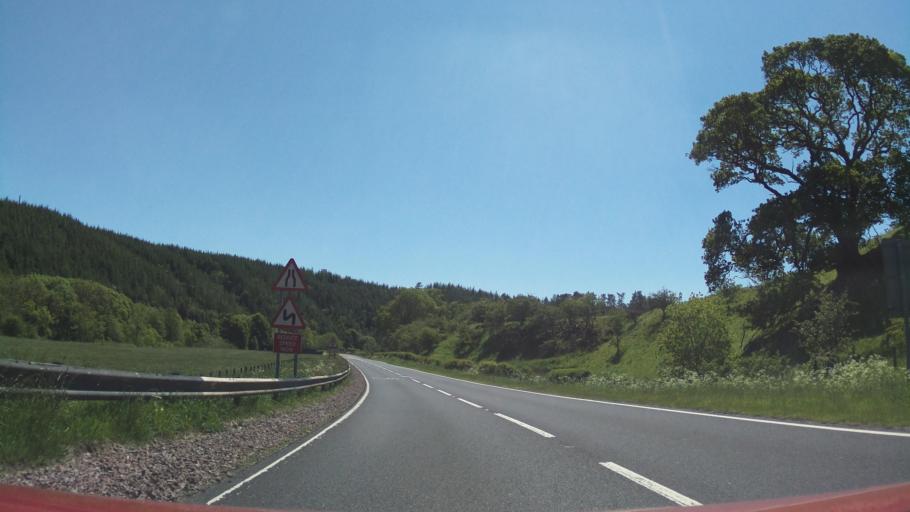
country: GB
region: Scotland
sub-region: Dumfries and Galloway
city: Langholm
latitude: 55.1654
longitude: -2.9934
